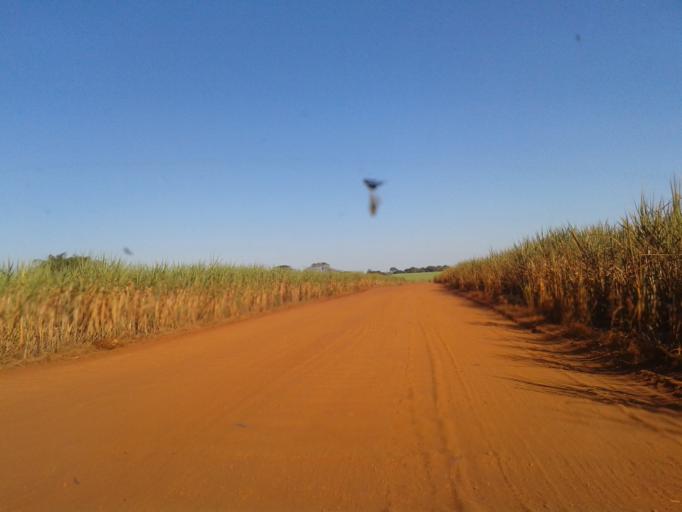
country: BR
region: Minas Gerais
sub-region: Santa Vitoria
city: Santa Vitoria
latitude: -18.8617
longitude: -50.0507
